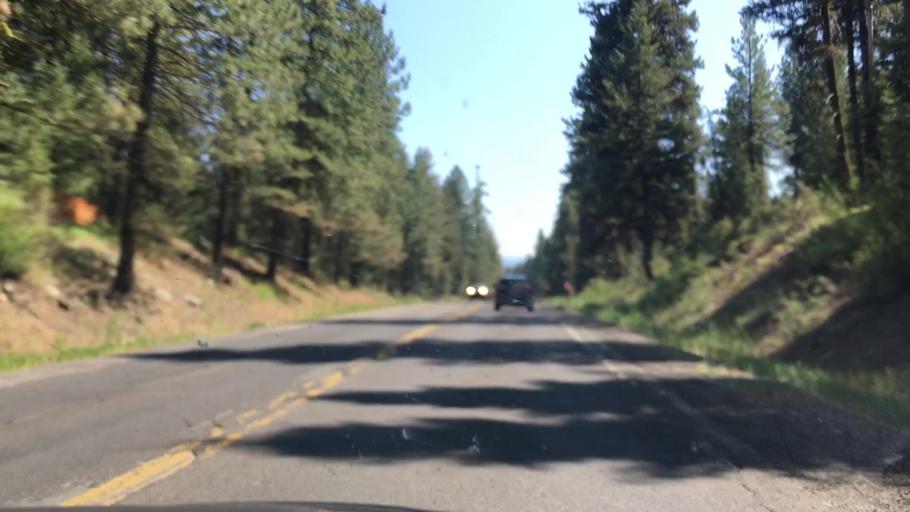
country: US
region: Idaho
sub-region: Valley County
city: McCall
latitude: 44.9225
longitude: -116.1396
